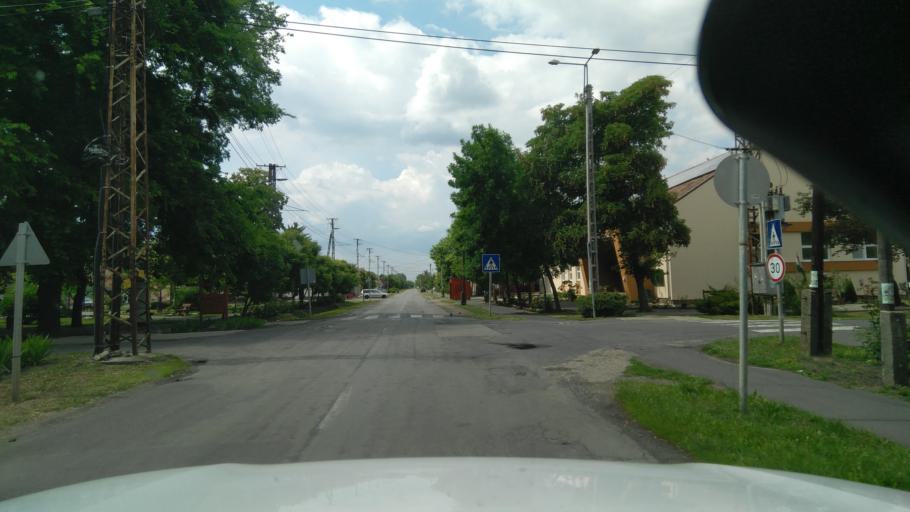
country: HU
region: Bekes
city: Magyarbanhegyes
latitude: 46.4567
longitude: 20.9643
